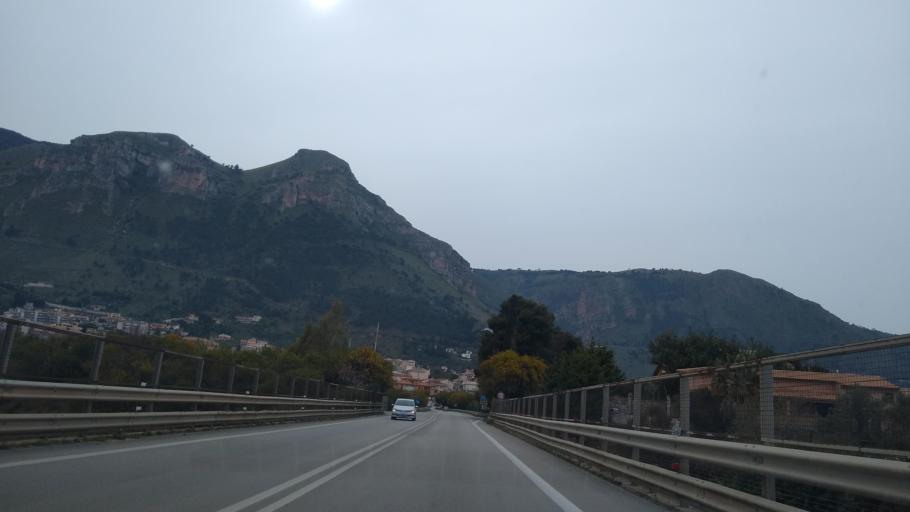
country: IT
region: Sicily
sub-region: Trapani
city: Castellammare del Golfo
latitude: 38.0160
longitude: 12.8963
